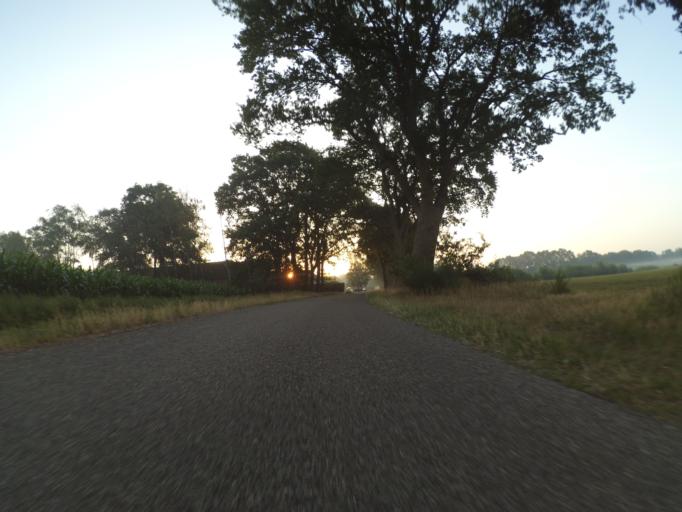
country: NL
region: Overijssel
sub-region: Gemeente Tubbergen
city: Tubbergen
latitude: 52.4033
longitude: 6.8252
